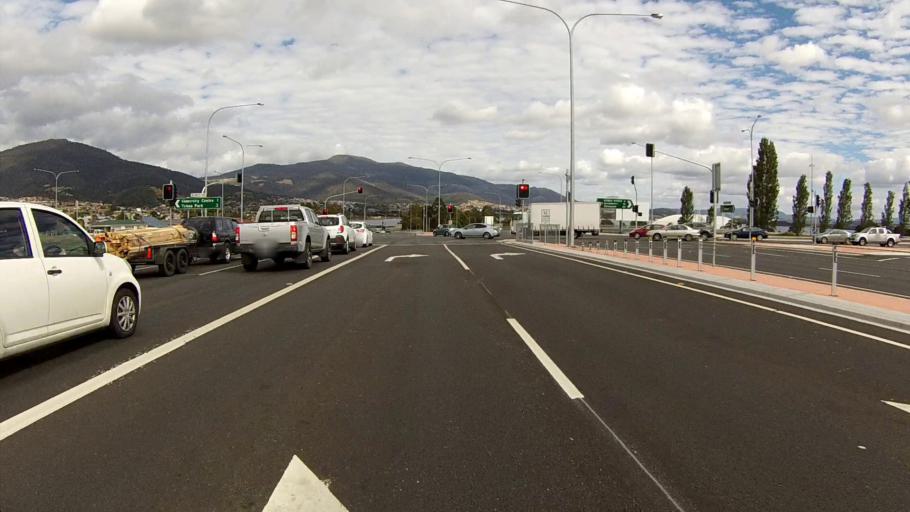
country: AU
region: Tasmania
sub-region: Glenorchy
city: Goodwood
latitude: -42.8282
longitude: 147.2857
